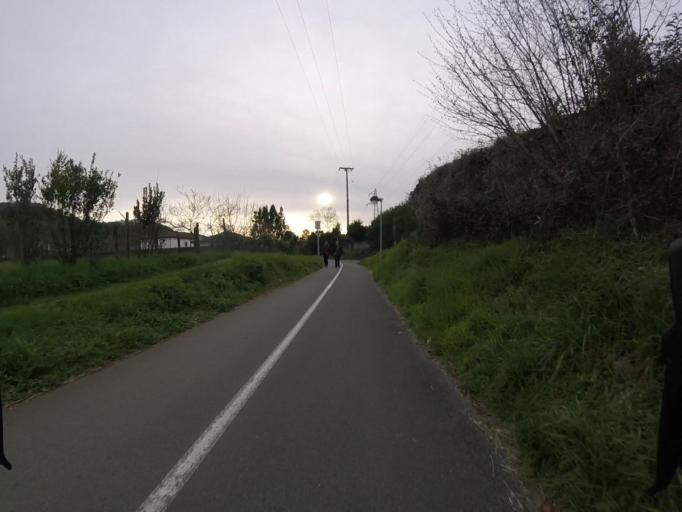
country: ES
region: Basque Country
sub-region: Provincia de Guipuzcoa
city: Lezo
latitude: 43.2946
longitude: -1.8532
